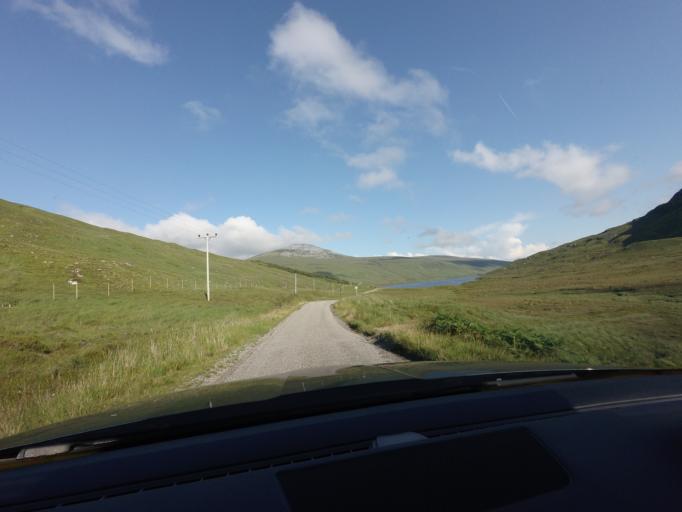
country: GB
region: Scotland
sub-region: Highland
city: Ullapool
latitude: 58.2580
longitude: -4.7791
